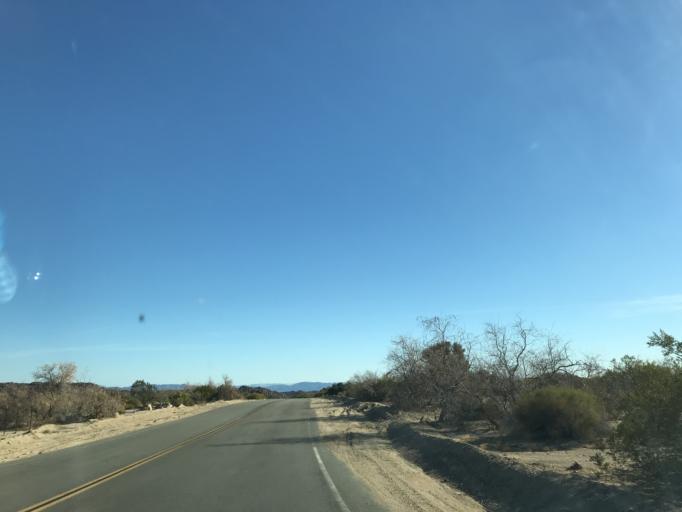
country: US
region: California
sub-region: Riverside County
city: Mecca
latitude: 33.7916
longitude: -115.7909
